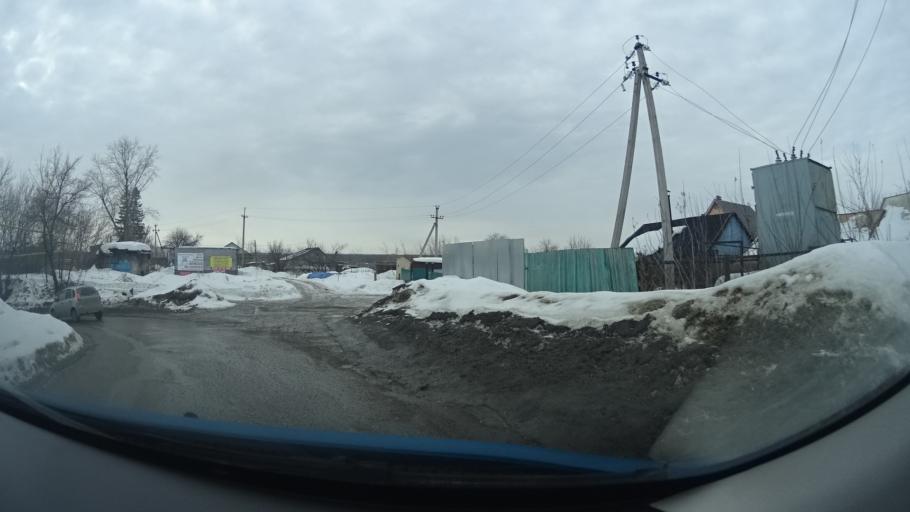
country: RU
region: Bashkortostan
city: Ufa
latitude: 54.6910
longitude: 55.9879
